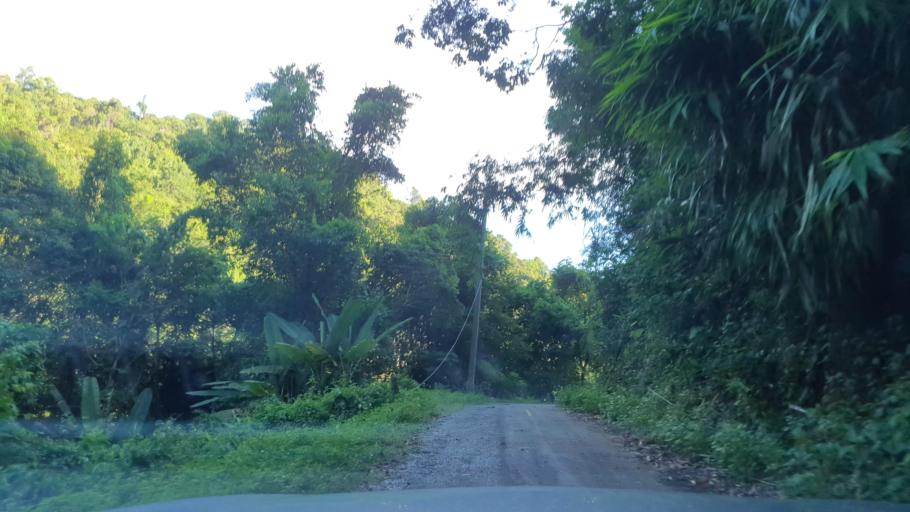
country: TH
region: Chiang Mai
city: Mae On
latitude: 18.8149
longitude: 99.3350
